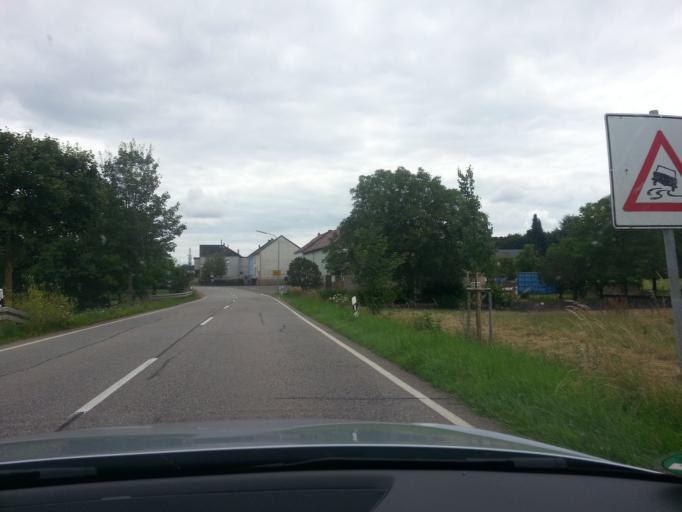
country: DE
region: Saarland
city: Orscholz
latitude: 49.4727
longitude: 6.4736
